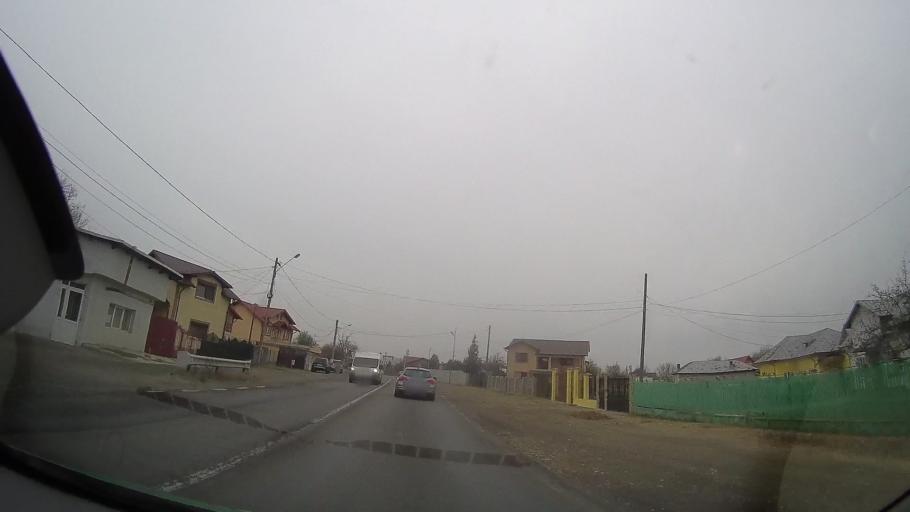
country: RO
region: Prahova
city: Ploiesti
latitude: 44.9652
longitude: 26.0308
